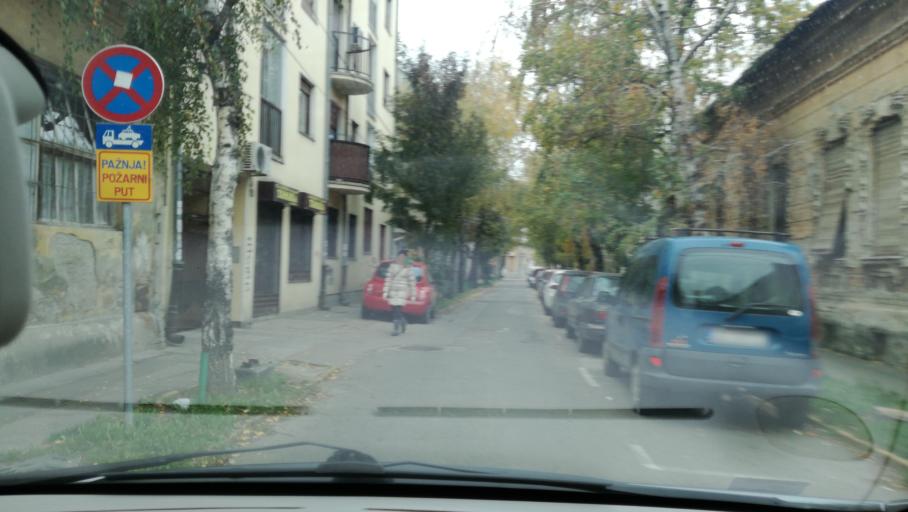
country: RS
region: Autonomna Pokrajina Vojvodina
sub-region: Juznobacki Okrug
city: Novi Sad
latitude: 45.2592
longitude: 19.8411
